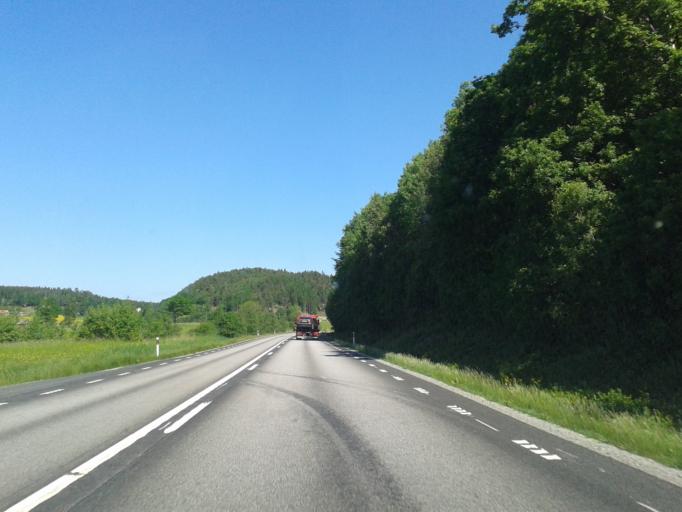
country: SE
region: Vaestra Goetaland
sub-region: Orust
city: Henan
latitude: 58.1987
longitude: 11.6897
